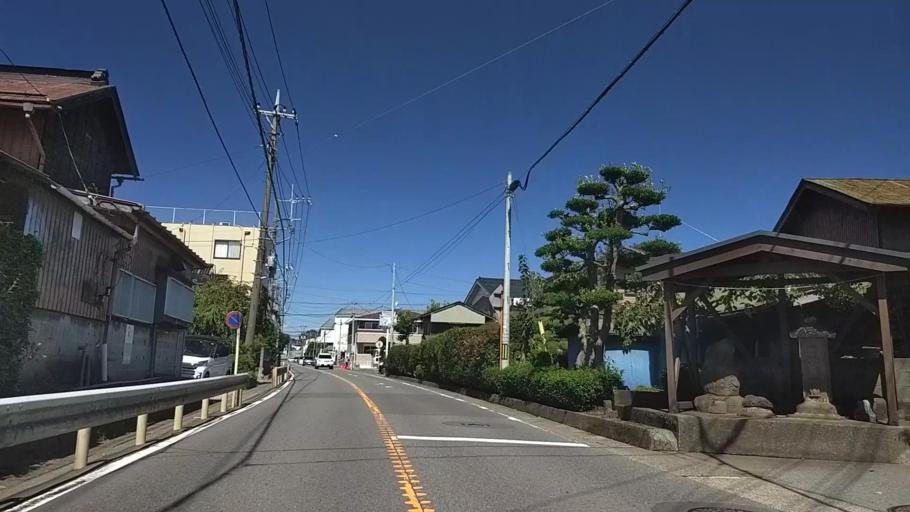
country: JP
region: Kanagawa
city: Zama
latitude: 35.5426
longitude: 139.3381
